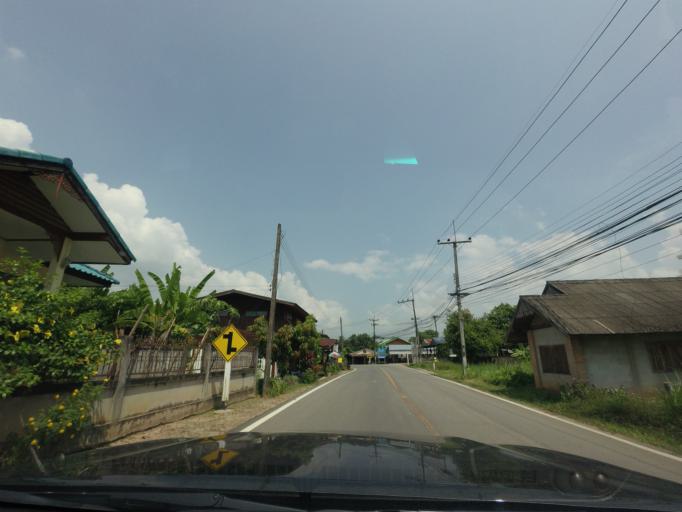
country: TH
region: Nan
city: Santi Suk
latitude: 18.9377
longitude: 100.9262
